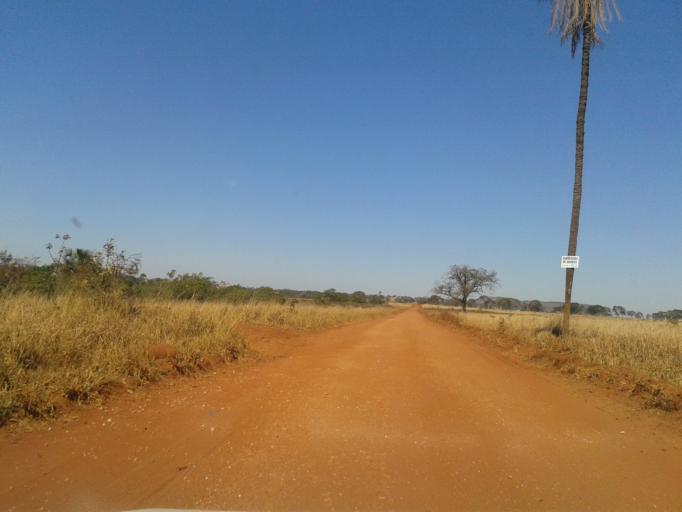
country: BR
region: Minas Gerais
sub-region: Santa Vitoria
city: Santa Vitoria
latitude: -19.1520
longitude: -50.1564
